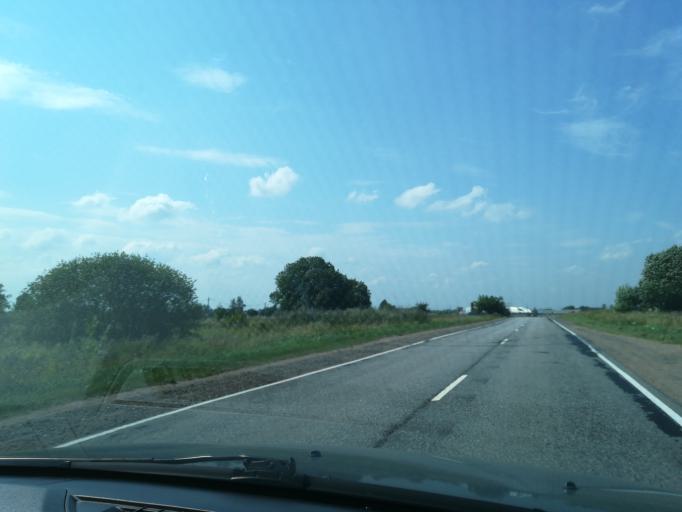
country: RU
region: Leningrad
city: Sista-Palkino
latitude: 59.5761
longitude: 28.7842
